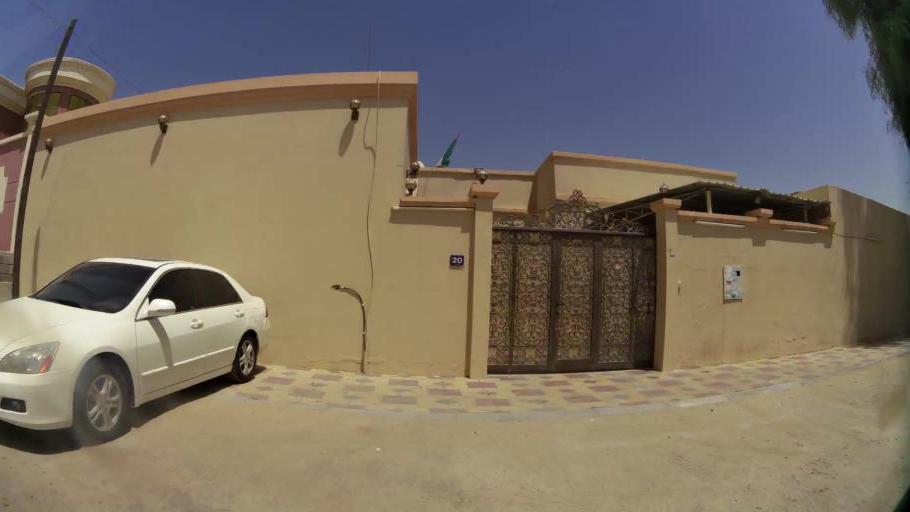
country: AE
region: Ajman
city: Ajman
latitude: 25.4039
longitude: 55.5111
